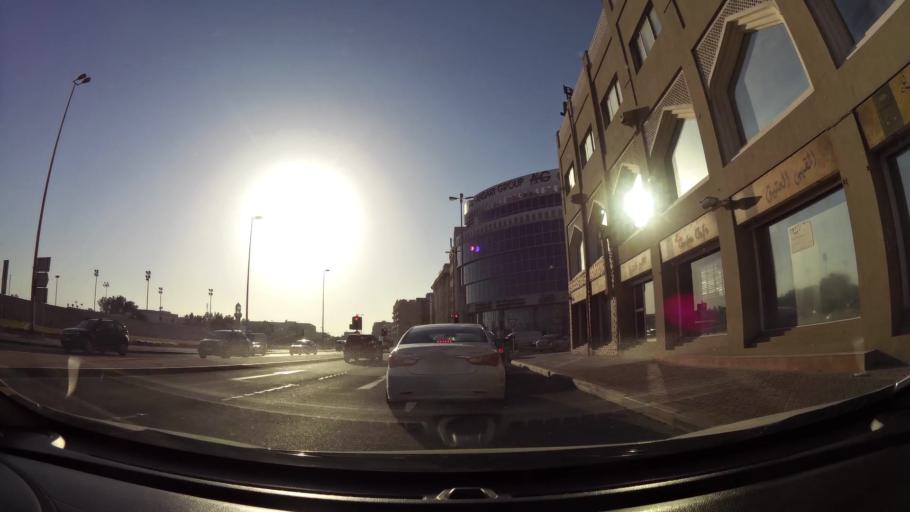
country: BH
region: Manama
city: Manama
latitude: 26.2243
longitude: 50.5969
